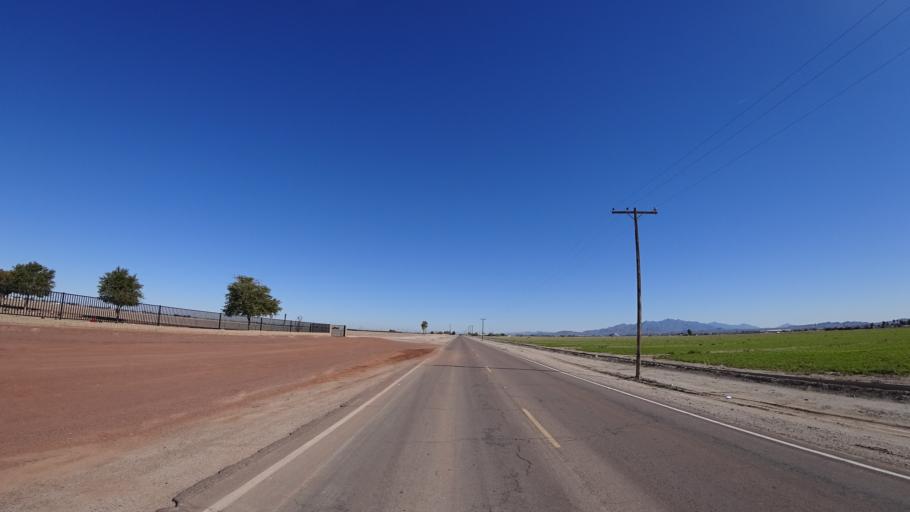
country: US
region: Arizona
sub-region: Maricopa County
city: Buckeye
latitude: 33.4067
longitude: -112.5461
